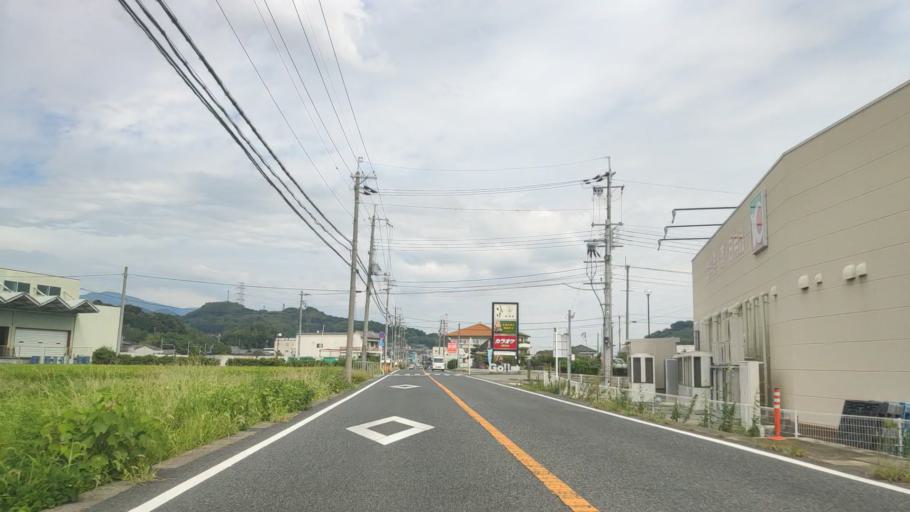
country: JP
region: Wakayama
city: Iwade
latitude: 34.2754
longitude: 135.4412
